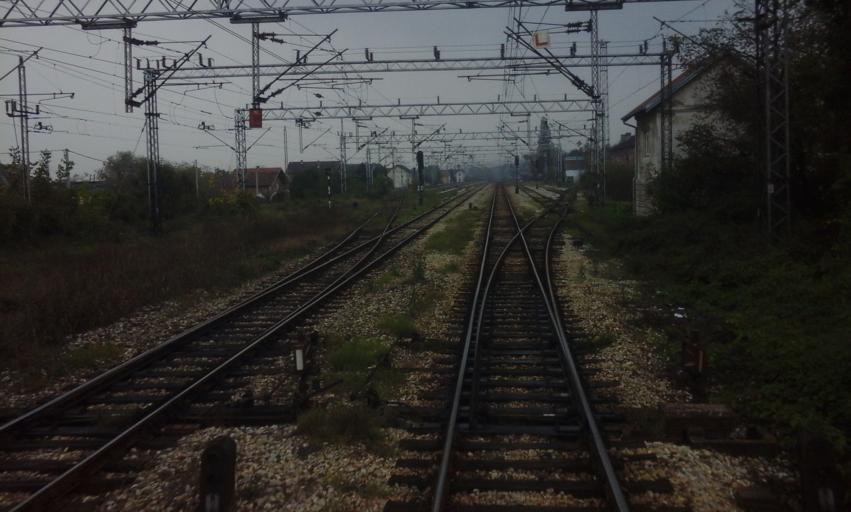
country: RS
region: Central Serbia
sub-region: Sumadijski Okrug
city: Batocina
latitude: 44.1619
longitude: 21.0996
